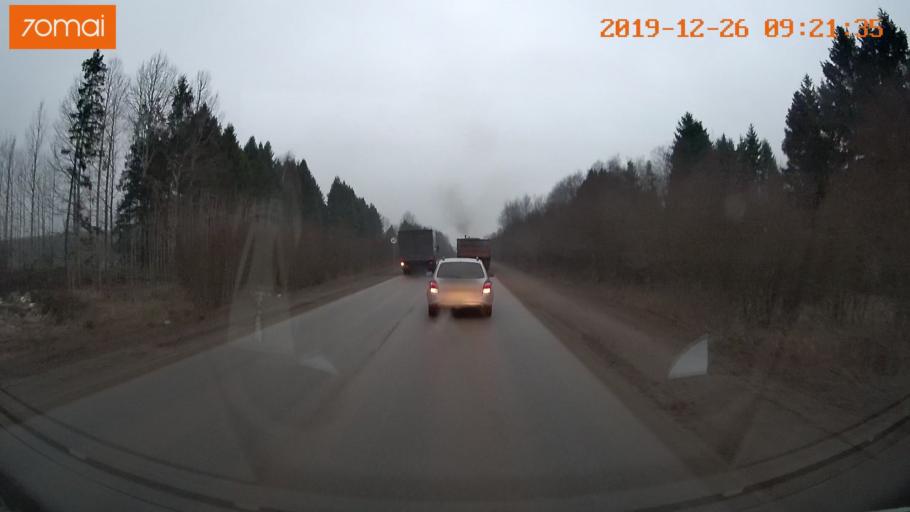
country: RU
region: Vologda
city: Gryazovets
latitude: 58.9710
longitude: 40.2238
